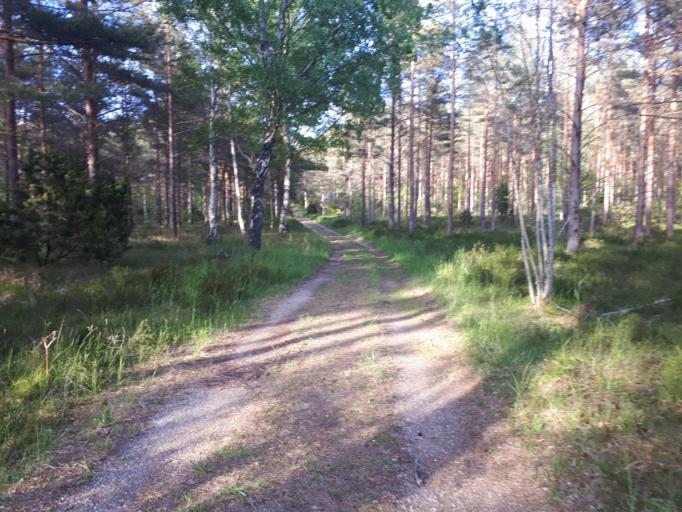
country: SE
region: Gotland
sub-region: Gotland
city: Visby
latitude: 57.6089
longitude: 18.2925
